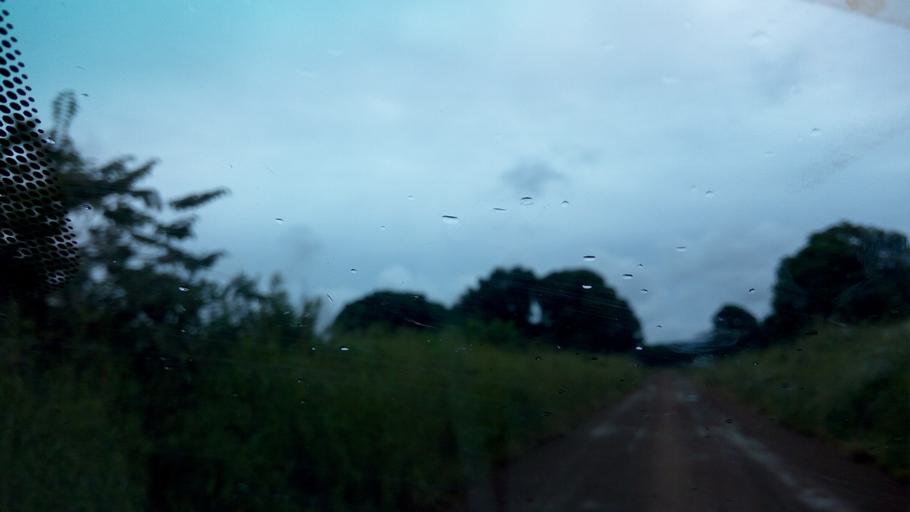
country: ZM
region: Luapula
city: Nchelenge
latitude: -8.9629
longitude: 28.4754
